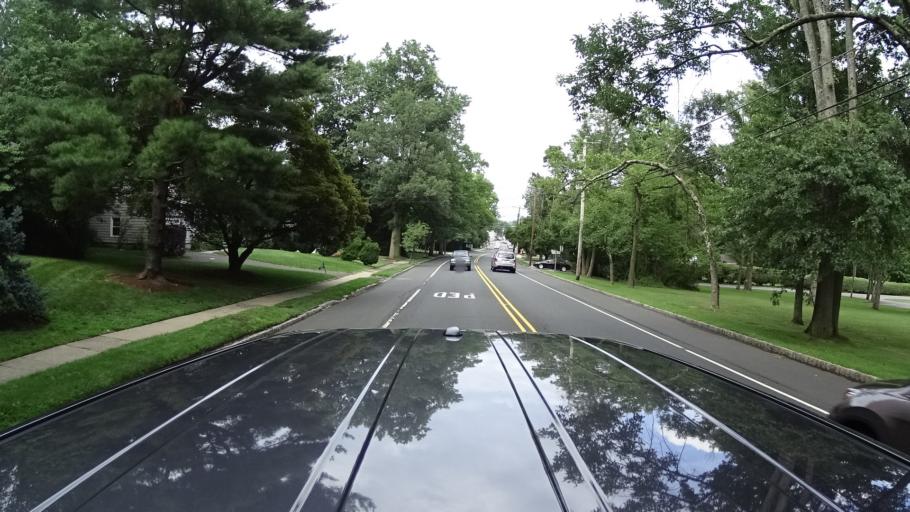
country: US
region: New Jersey
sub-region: Union County
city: New Providence
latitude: 40.7042
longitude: -74.4104
